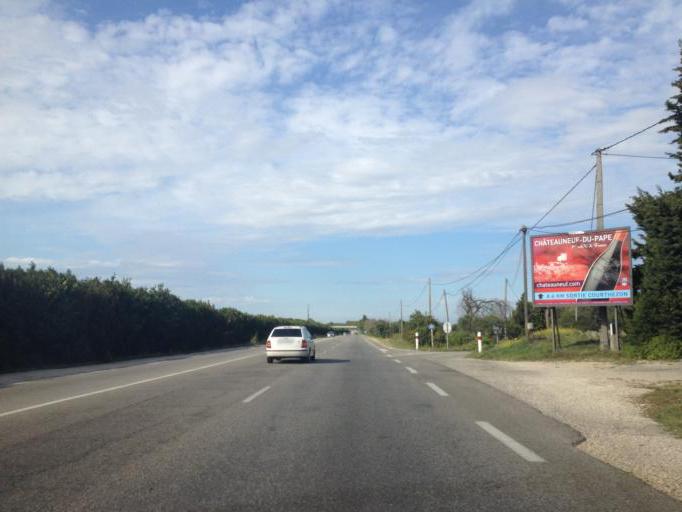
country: FR
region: Provence-Alpes-Cote d'Azur
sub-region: Departement du Vaucluse
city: Bedarrides
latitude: 44.0513
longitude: 4.8886
